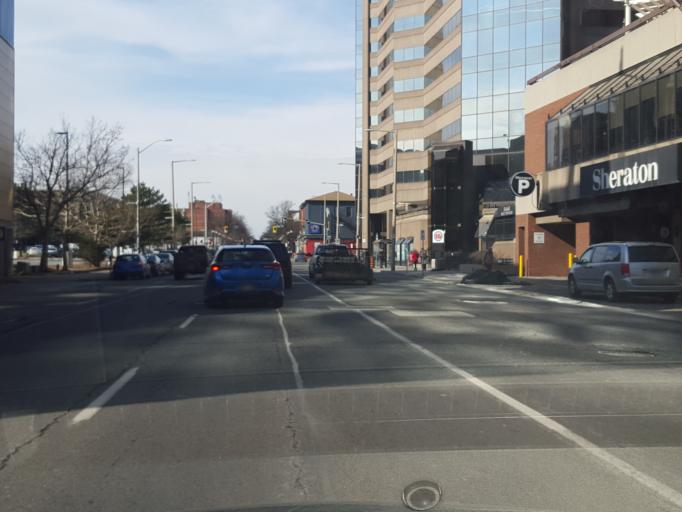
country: CA
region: Ontario
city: Hamilton
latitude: 43.2574
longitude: -79.8720
